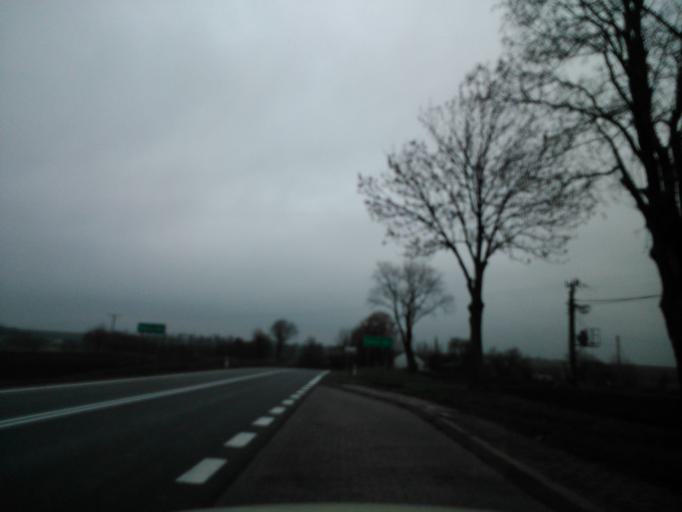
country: PL
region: Swietokrzyskie
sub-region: Powiat opatowski
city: Wojciechowice
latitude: 50.8173
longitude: 21.5833
